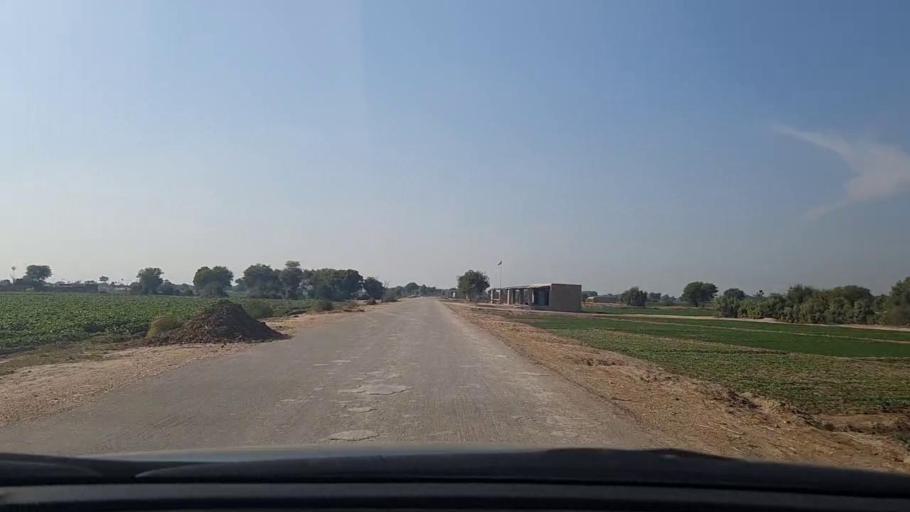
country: PK
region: Sindh
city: Daulatpur
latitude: 26.3137
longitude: 68.0703
